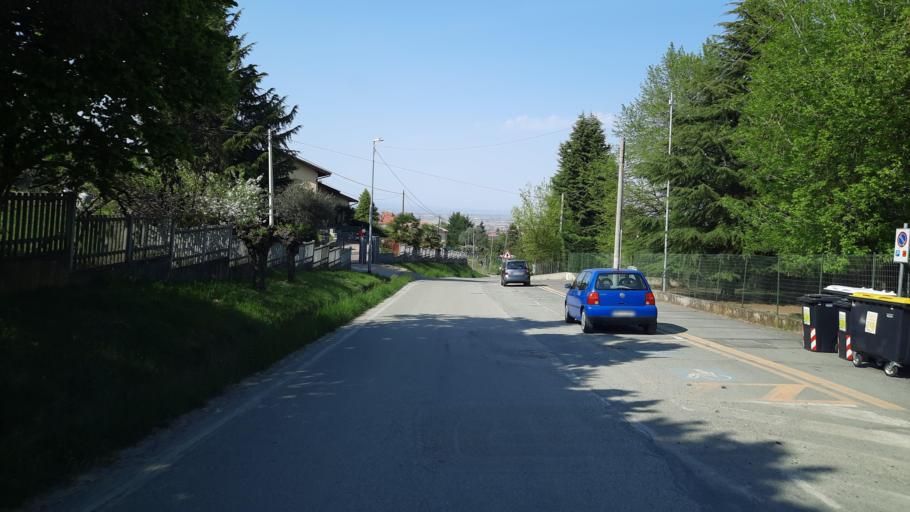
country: IT
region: Piedmont
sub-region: Provincia di Torino
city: Valentino
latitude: 45.1529
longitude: 8.0933
